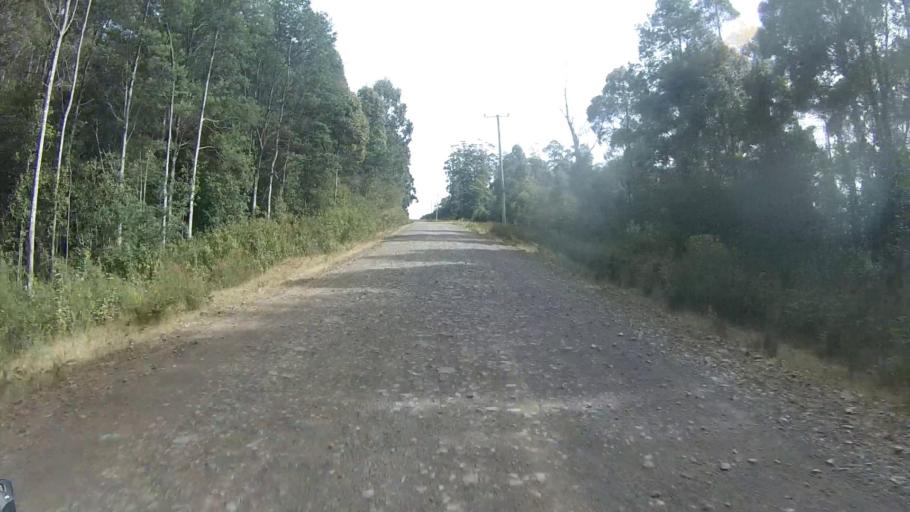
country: AU
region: Tasmania
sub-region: Sorell
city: Sorell
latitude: -42.7690
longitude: 147.8311
